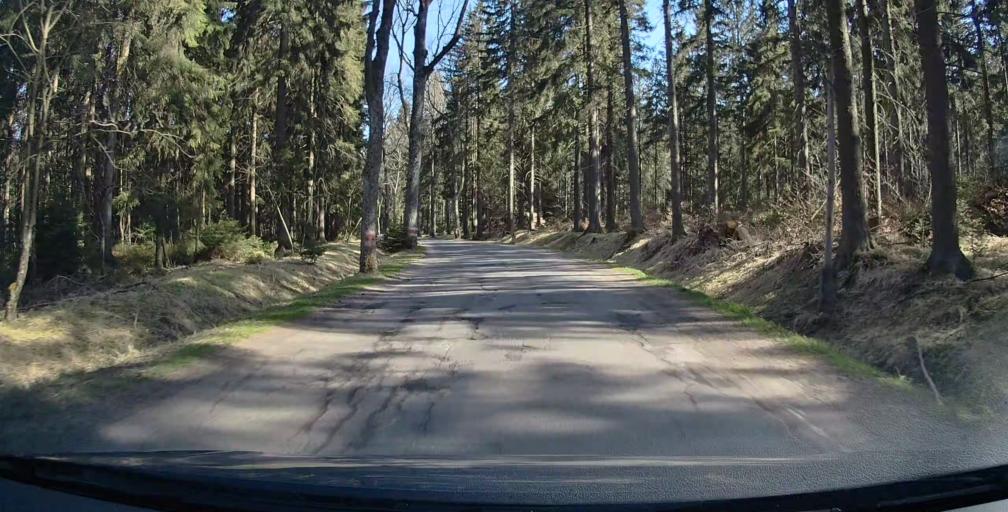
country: CZ
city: Machov
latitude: 50.4718
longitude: 16.3386
